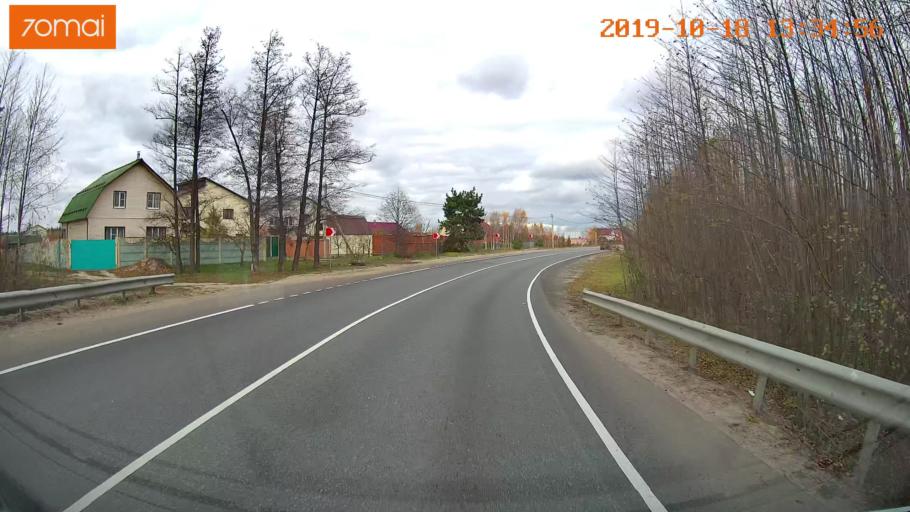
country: RU
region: Rjazan
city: Solotcha
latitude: 54.8574
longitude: 39.9614
